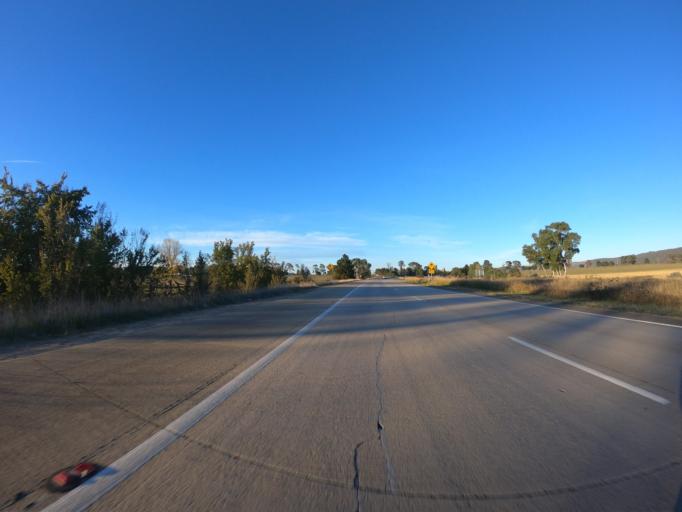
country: AU
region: New South Wales
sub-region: Yass Valley
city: Gundaroo
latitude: -34.9335
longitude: 149.4221
